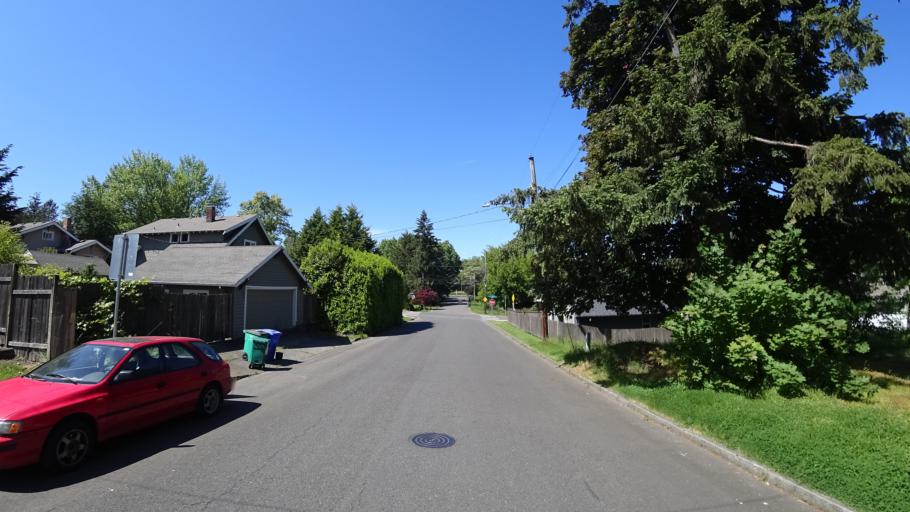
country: US
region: Oregon
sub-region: Washington County
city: Metzger
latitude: 45.4516
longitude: -122.7180
